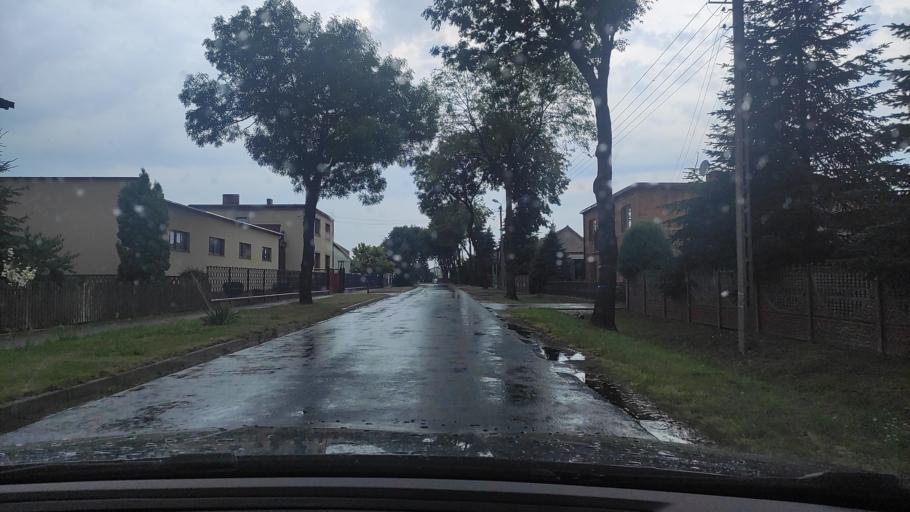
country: PL
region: Greater Poland Voivodeship
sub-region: Powiat poznanski
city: Kleszczewo
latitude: 52.2951
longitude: 17.1562
